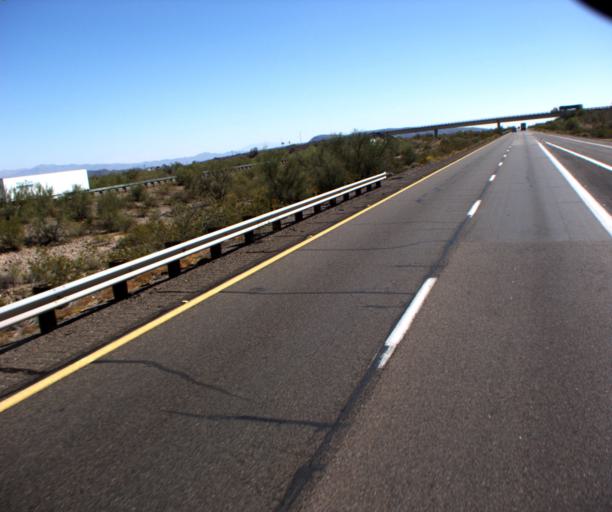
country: US
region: Arizona
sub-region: La Paz County
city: Quartzsite
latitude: 33.6619
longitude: -114.0145
